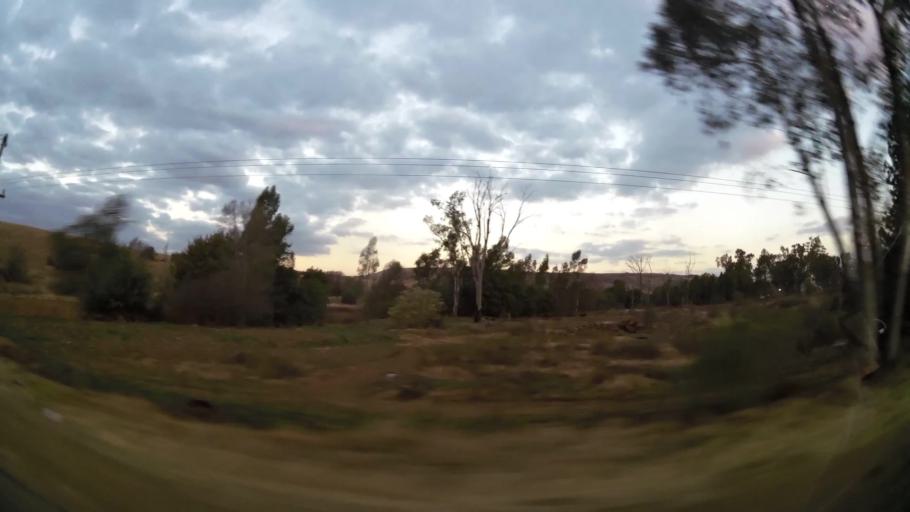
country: ZA
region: Gauteng
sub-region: West Rand District Municipality
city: Krugersdorp
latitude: -26.0406
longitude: 27.7205
